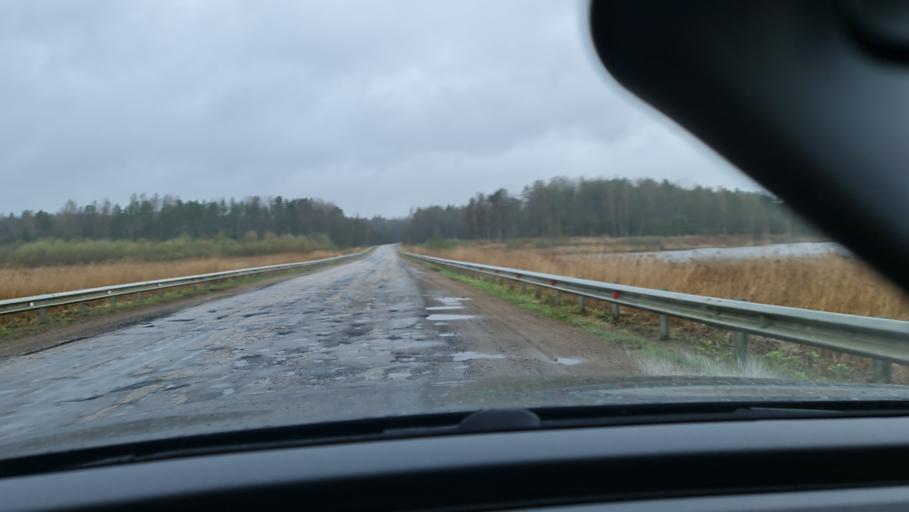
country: RU
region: Novgorod
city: Valday
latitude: 58.0394
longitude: 32.9034
